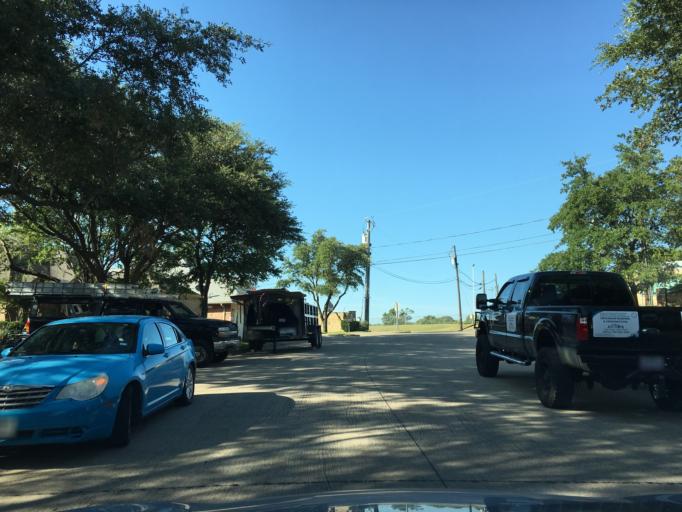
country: US
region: Texas
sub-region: Dallas County
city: Garland
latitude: 32.8572
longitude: -96.7034
